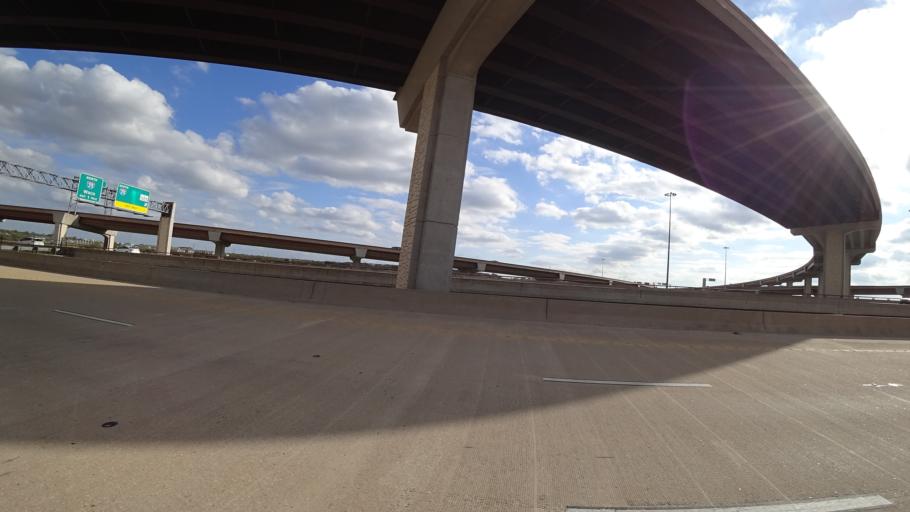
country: US
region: Texas
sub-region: Travis County
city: Wells Branch
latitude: 30.4768
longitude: -97.7011
